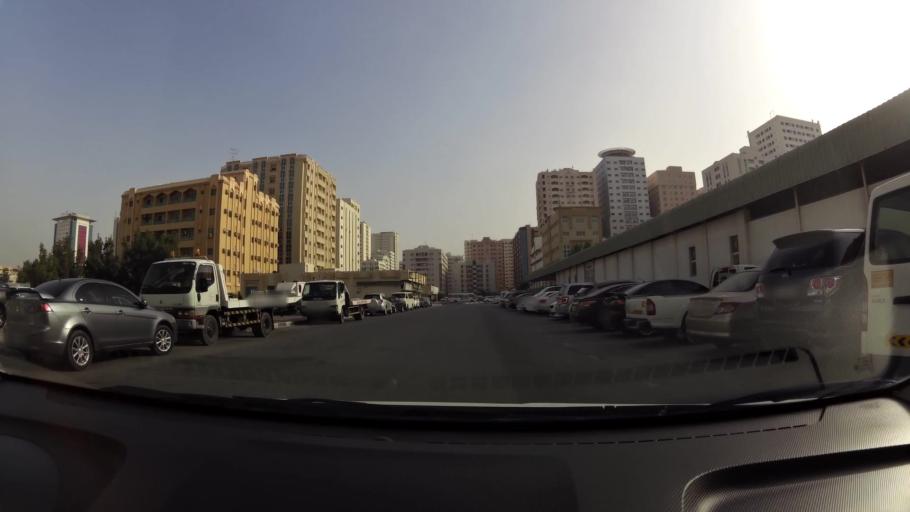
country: AE
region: Ash Shariqah
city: Sharjah
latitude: 25.3403
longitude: 55.3988
